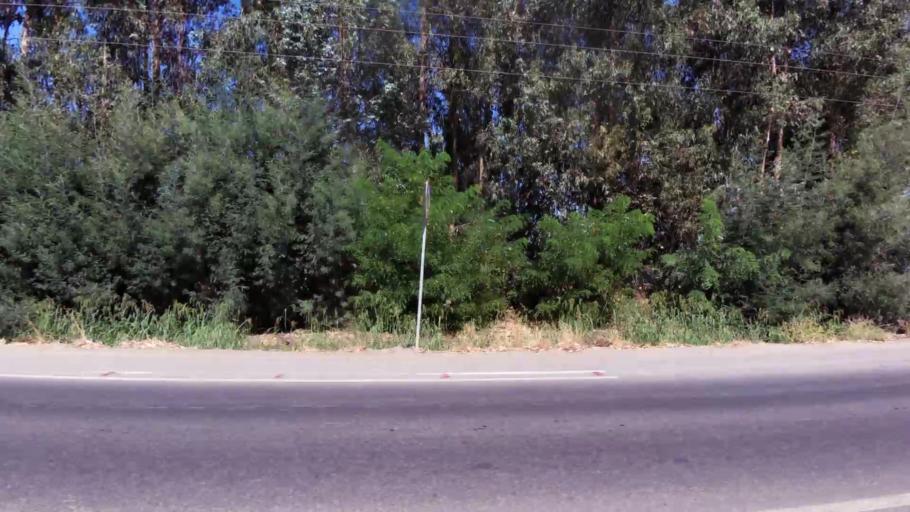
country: CL
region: Maule
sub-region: Provincia de Talca
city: Talca
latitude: -35.4375
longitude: -71.6117
